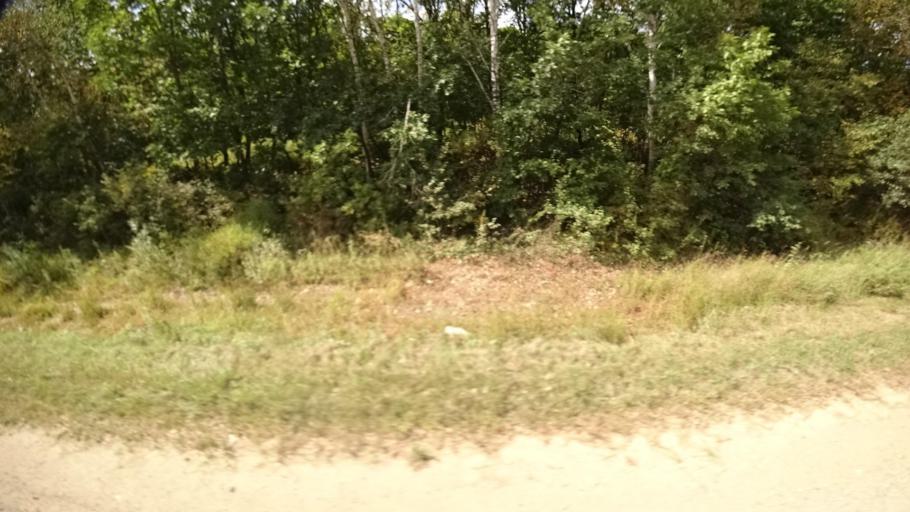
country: RU
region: Primorskiy
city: Yakovlevka
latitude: 44.6554
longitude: 133.5969
